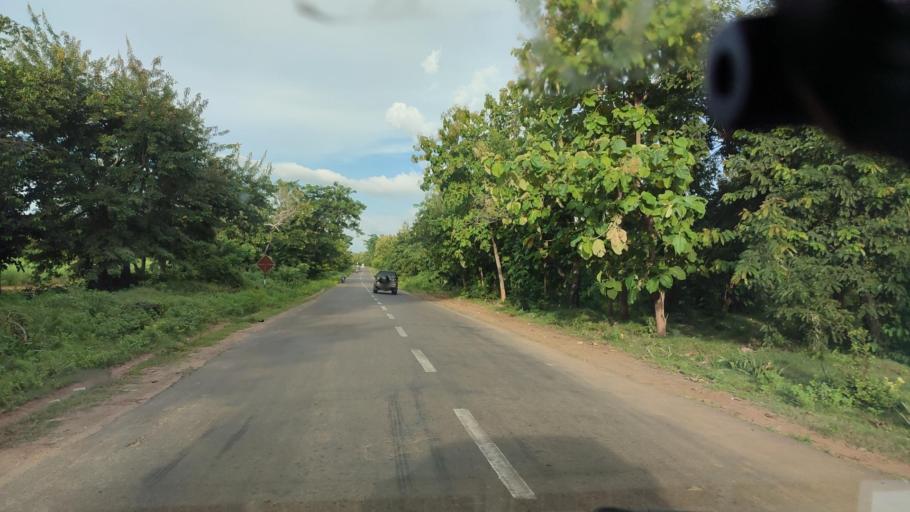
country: MM
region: Magway
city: Chauk
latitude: 20.8167
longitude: 95.0562
